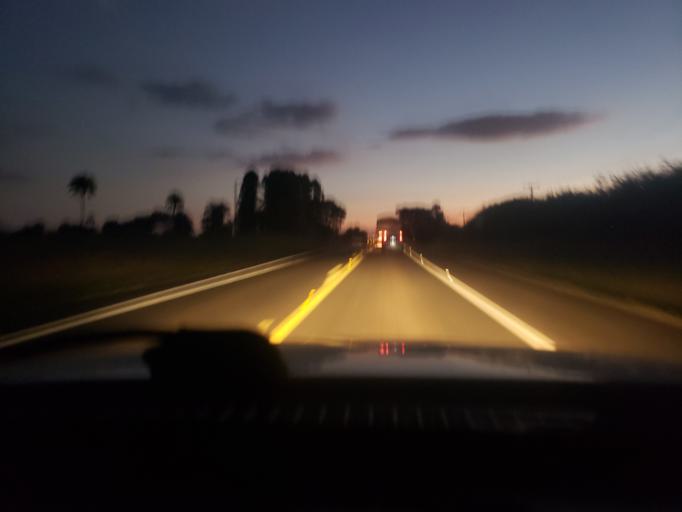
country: BR
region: Sao Paulo
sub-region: Conchal
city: Conchal
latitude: -22.3292
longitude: -47.1502
